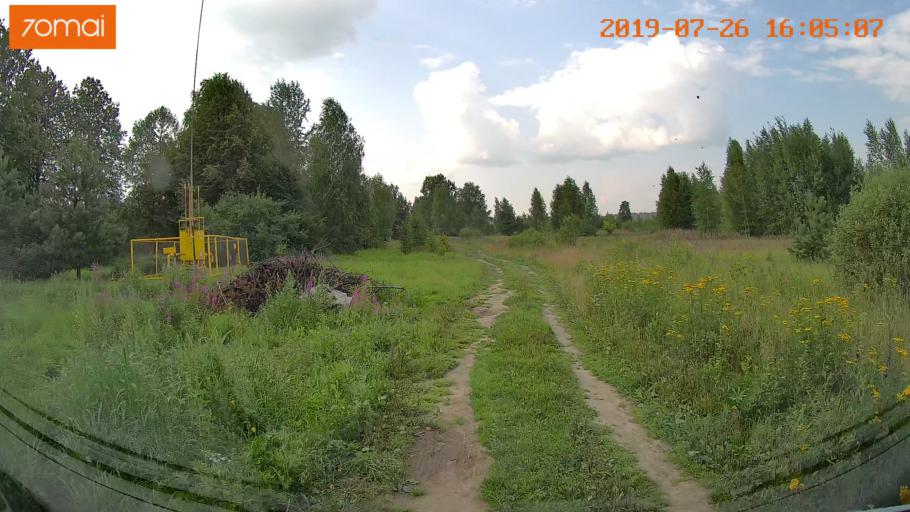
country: RU
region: Ivanovo
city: Bogorodskoye
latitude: 57.0576
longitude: 41.0577
